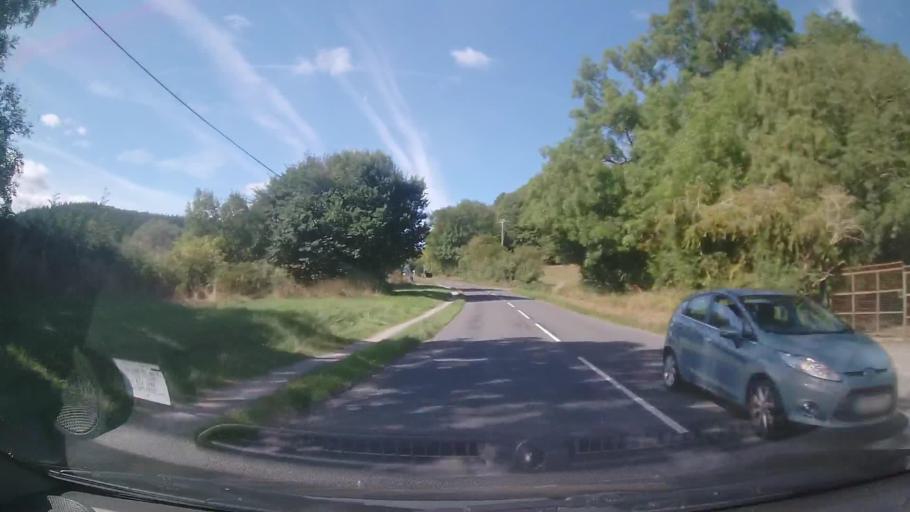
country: GB
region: Wales
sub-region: Sir Powys
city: Hay
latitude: 52.0837
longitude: -3.1456
